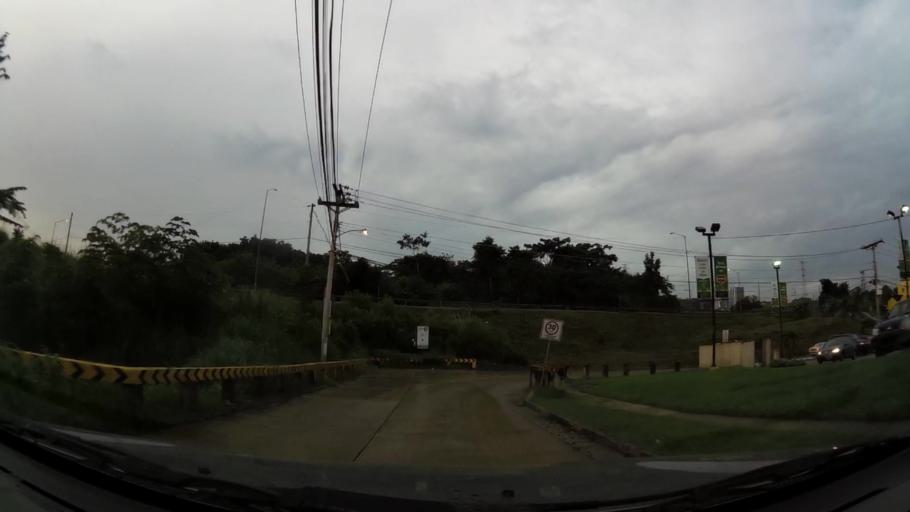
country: PA
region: Panama
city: Panama
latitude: 9.0383
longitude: -79.5302
